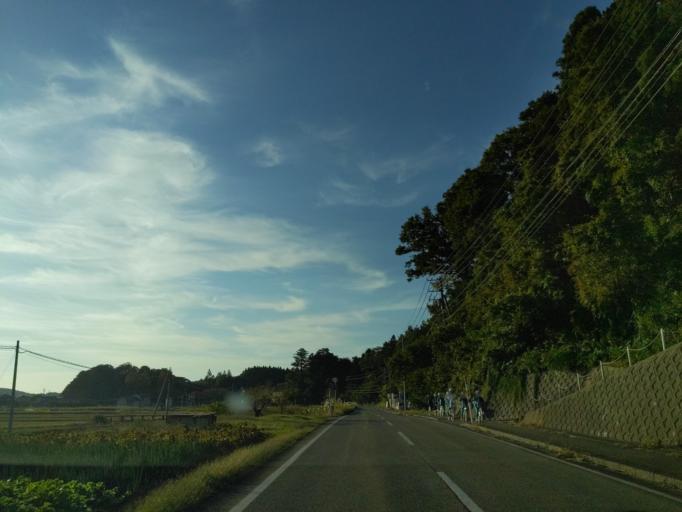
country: JP
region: Niigata
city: Nagaoka
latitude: 37.5787
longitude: 138.7653
